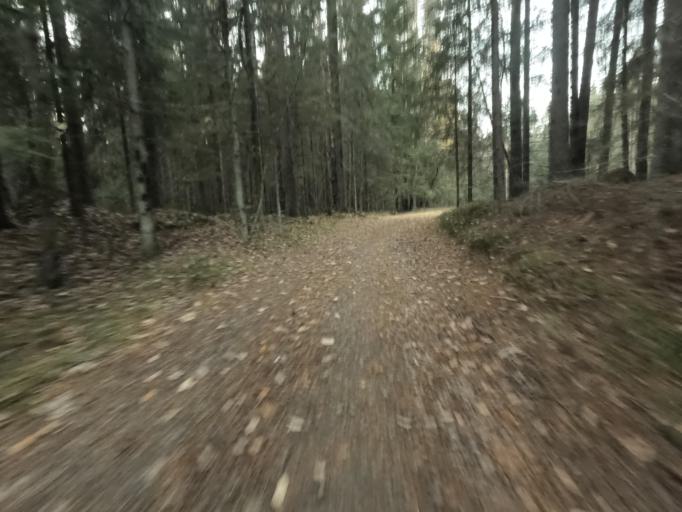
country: RU
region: Leningrad
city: Leninskoye
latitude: 60.1962
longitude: 29.8486
